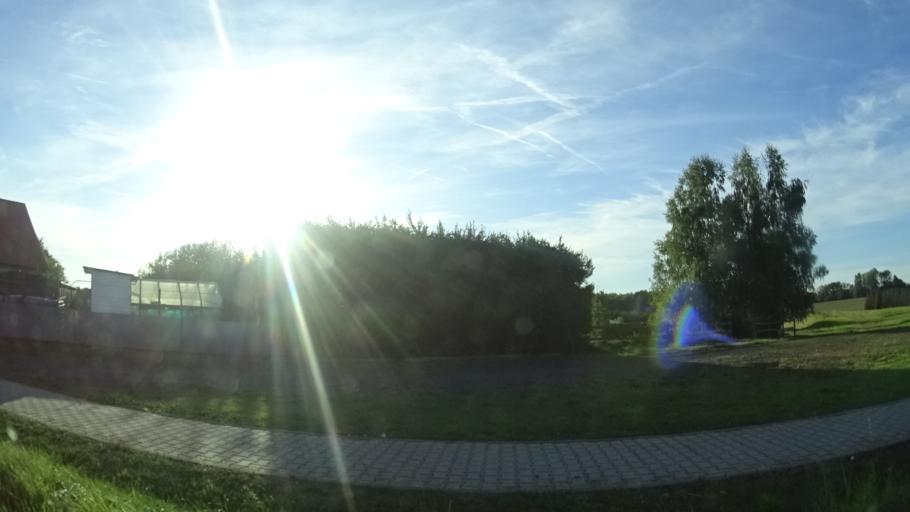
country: DE
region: Hesse
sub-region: Regierungsbezirk Darmstadt
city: Wachtersbach
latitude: 50.2885
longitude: 9.2616
